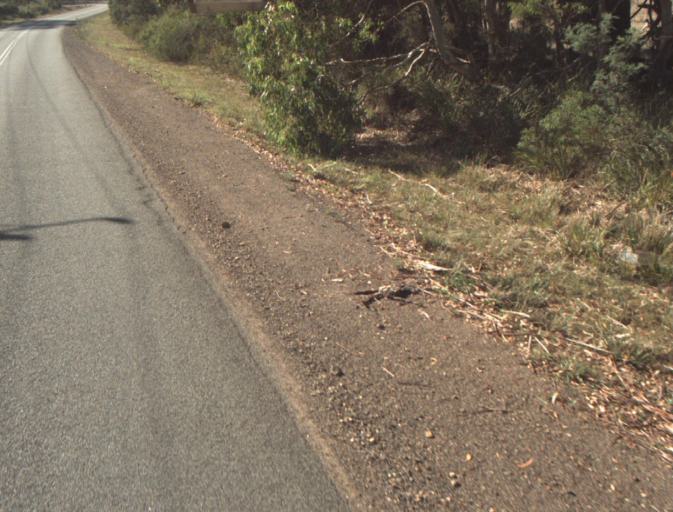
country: AU
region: Tasmania
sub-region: Launceston
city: Mayfield
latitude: -41.2839
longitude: 147.1262
